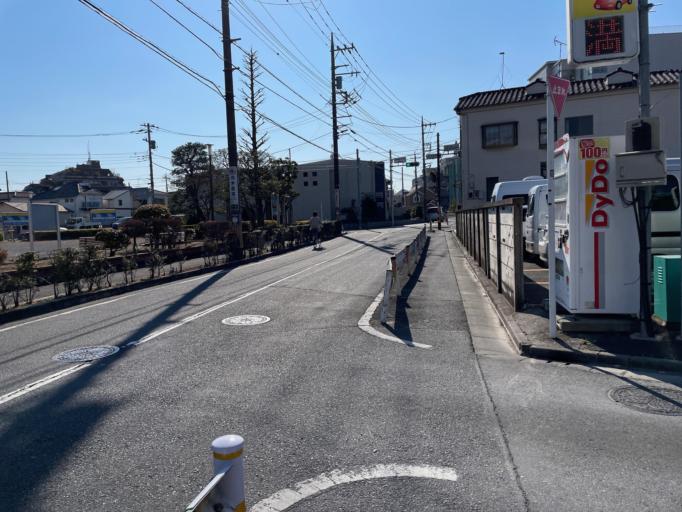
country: JP
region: Saitama
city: Soka
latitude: 35.7964
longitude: 139.7818
